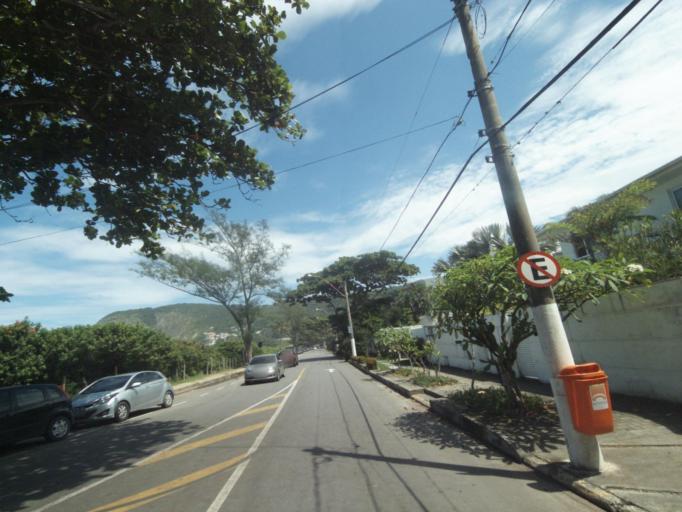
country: BR
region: Rio de Janeiro
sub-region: Niteroi
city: Niteroi
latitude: -22.9739
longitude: -43.0328
